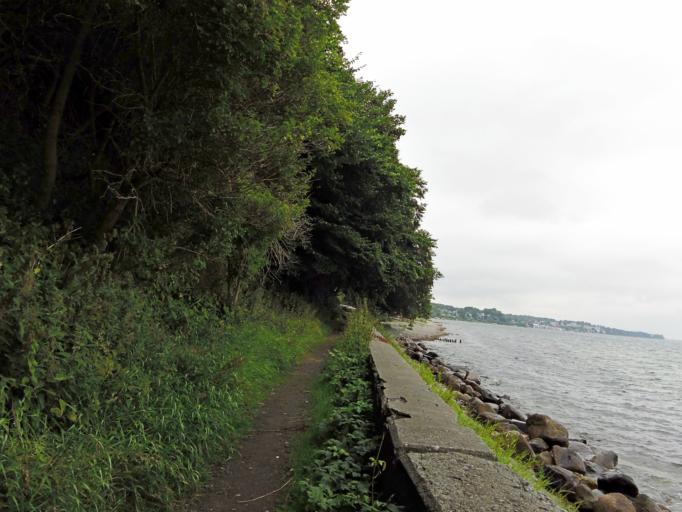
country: DK
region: Capital Region
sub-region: Gentofte Kommune
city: Charlottenlund
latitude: 55.8055
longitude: 12.5850
